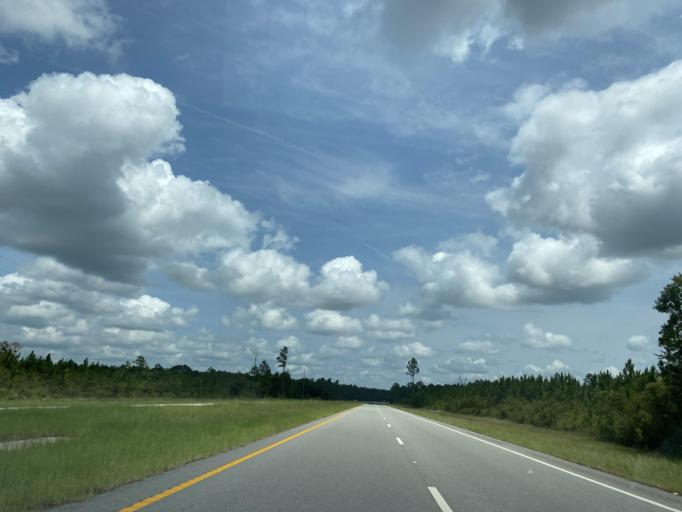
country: US
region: Georgia
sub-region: Ware County
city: Deenwood
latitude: 31.2728
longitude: -82.4424
